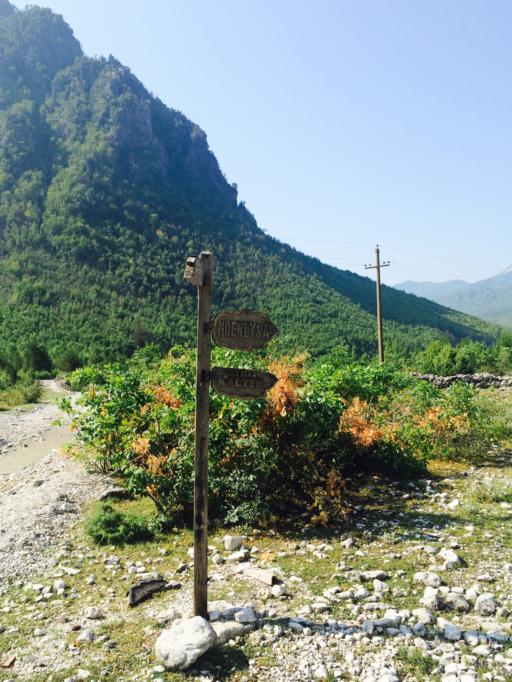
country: AL
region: Shkoder
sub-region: Rrethi i Shkodres
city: Nicaj-Shale
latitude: 42.3571
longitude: 19.7787
